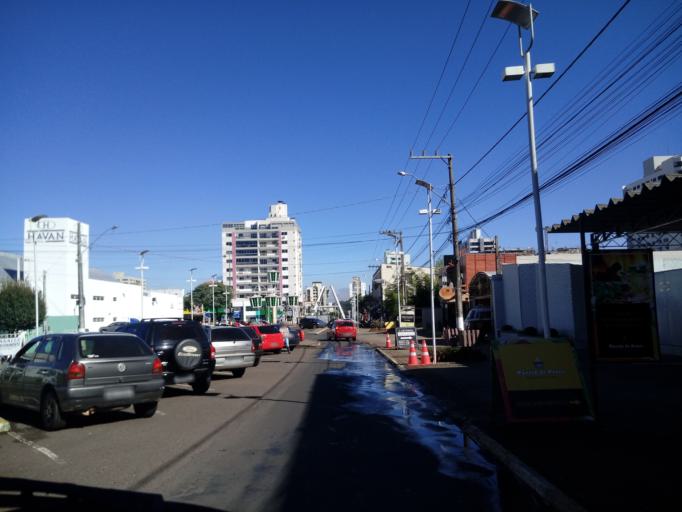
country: BR
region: Santa Catarina
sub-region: Chapeco
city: Chapeco
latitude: -27.0988
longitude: -52.6144
